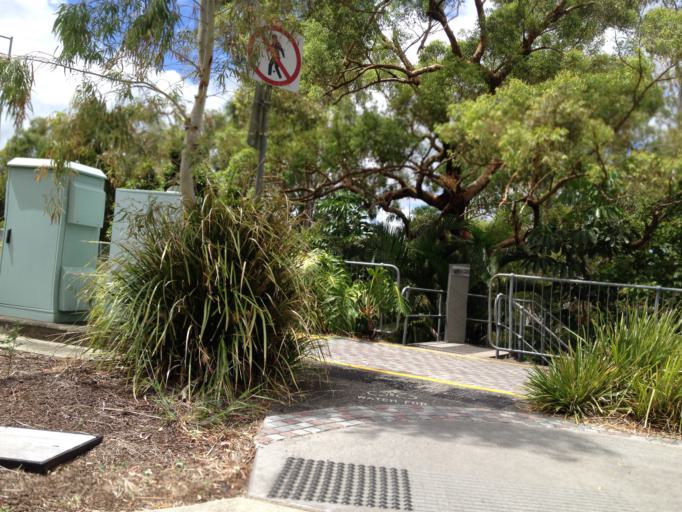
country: AU
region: Queensland
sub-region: Brisbane
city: Woolloongabba
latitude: -27.4980
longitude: 153.0252
